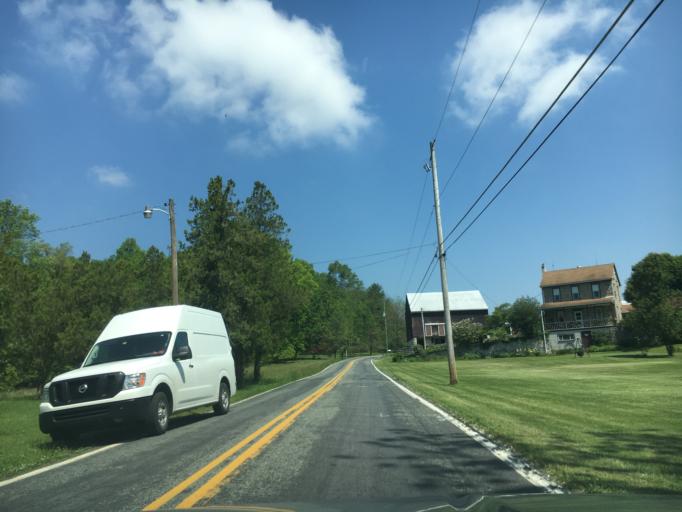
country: US
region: Pennsylvania
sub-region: Berks County
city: Fleetwood
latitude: 40.4509
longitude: -75.7811
